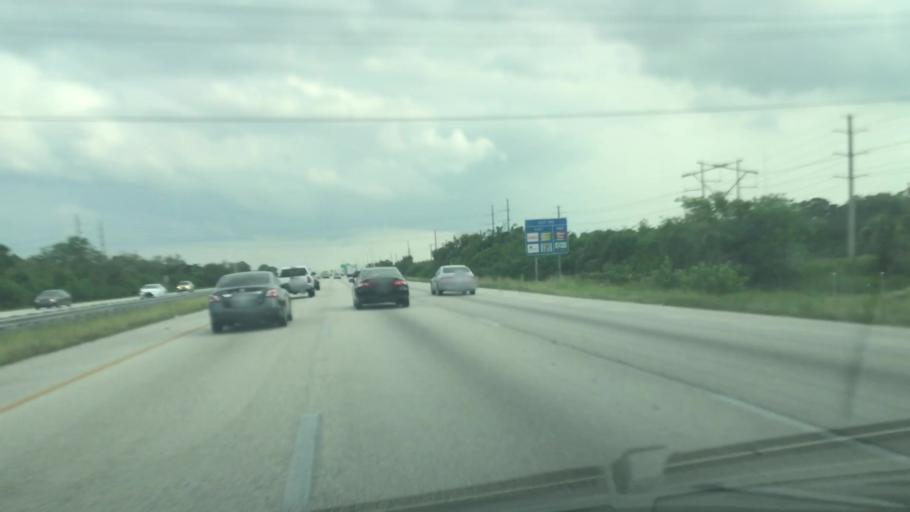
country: US
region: Florida
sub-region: Brevard County
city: June Park
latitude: 28.1309
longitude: -80.7062
